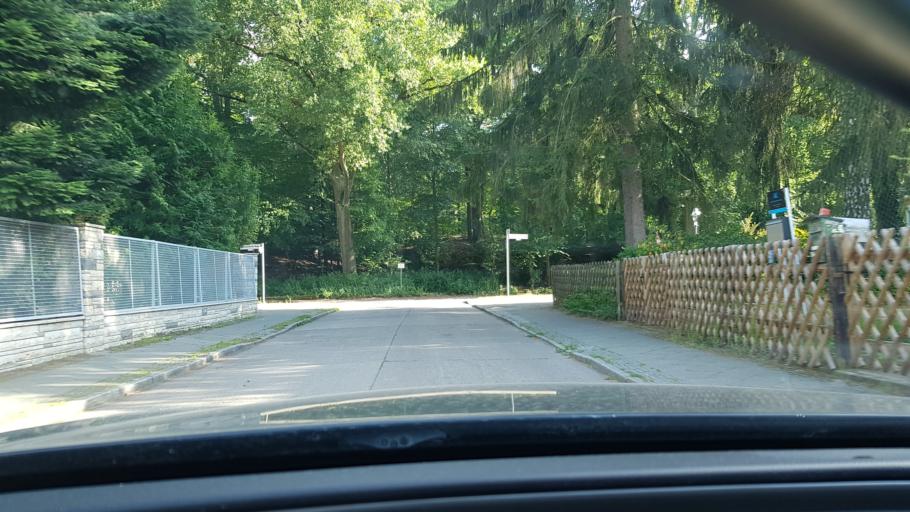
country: DE
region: Berlin
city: Frohnau
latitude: 52.6106
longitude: 13.2894
